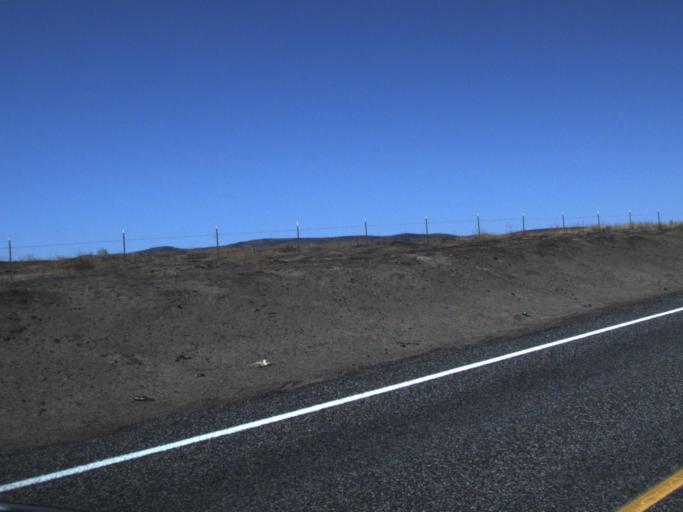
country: US
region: Washington
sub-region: Grant County
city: Desert Aire
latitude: 46.5712
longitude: -119.7270
